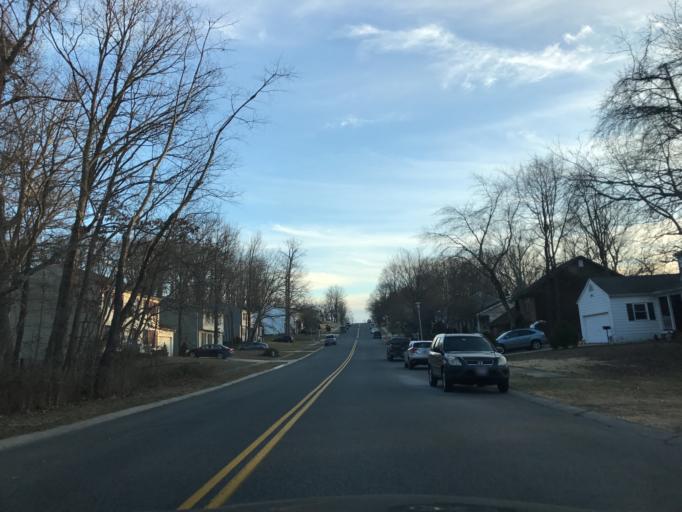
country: US
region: Maryland
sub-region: Harford County
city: Edgewood
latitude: 39.4032
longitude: -76.3445
